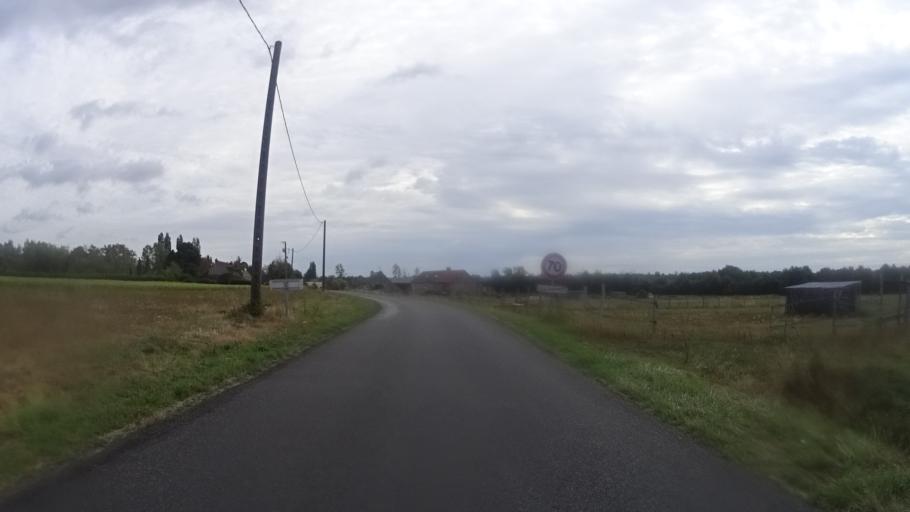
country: FR
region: Centre
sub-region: Departement du Loiret
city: Vitry-aux-Loges
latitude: 47.9933
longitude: 2.2173
